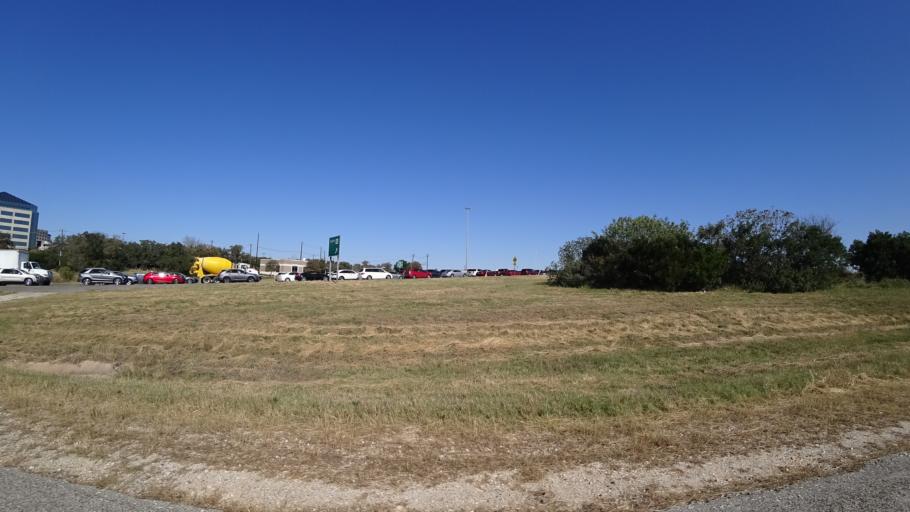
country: US
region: Texas
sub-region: Williamson County
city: Jollyville
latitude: 30.3883
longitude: -97.7471
